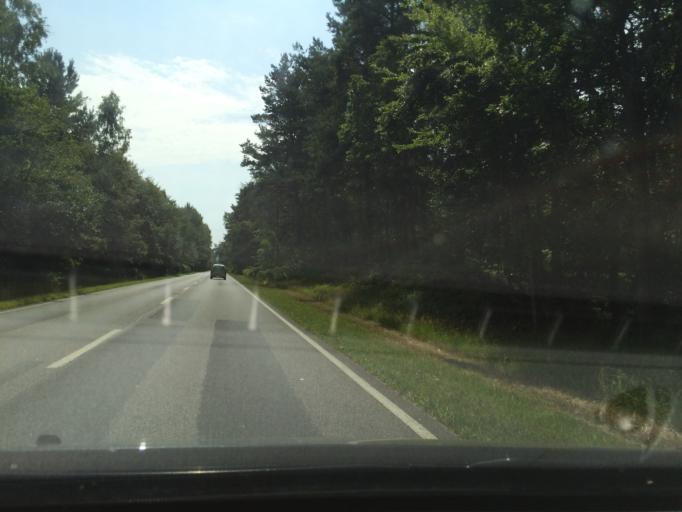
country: DE
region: Mecklenburg-Vorpommern
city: Ostseebad Binz
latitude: 54.4219
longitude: 13.5823
